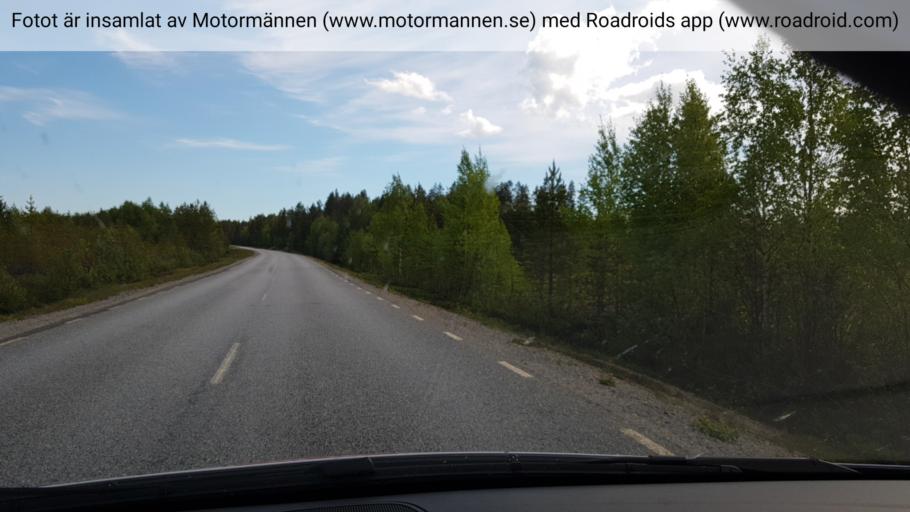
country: SE
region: Vaesterbotten
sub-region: Umea Kommun
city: Saevar
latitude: 63.9526
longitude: 20.5113
